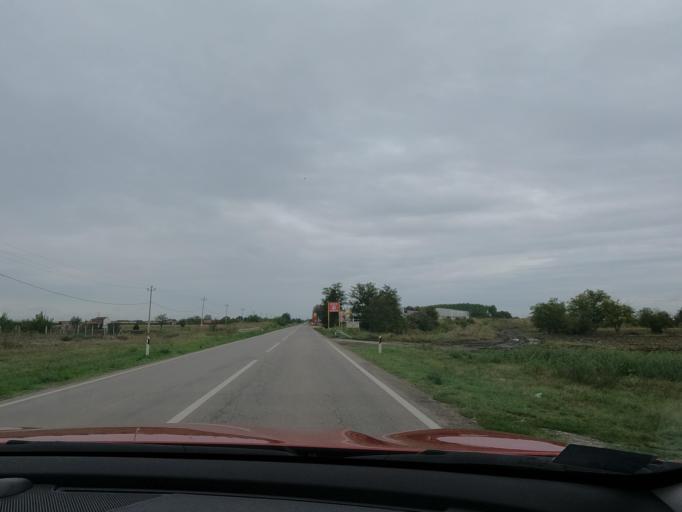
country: RS
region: Autonomna Pokrajina Vojvodina
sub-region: Severnobanatski Okrug
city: Kikinda
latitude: 45.7857
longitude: 20.4326
